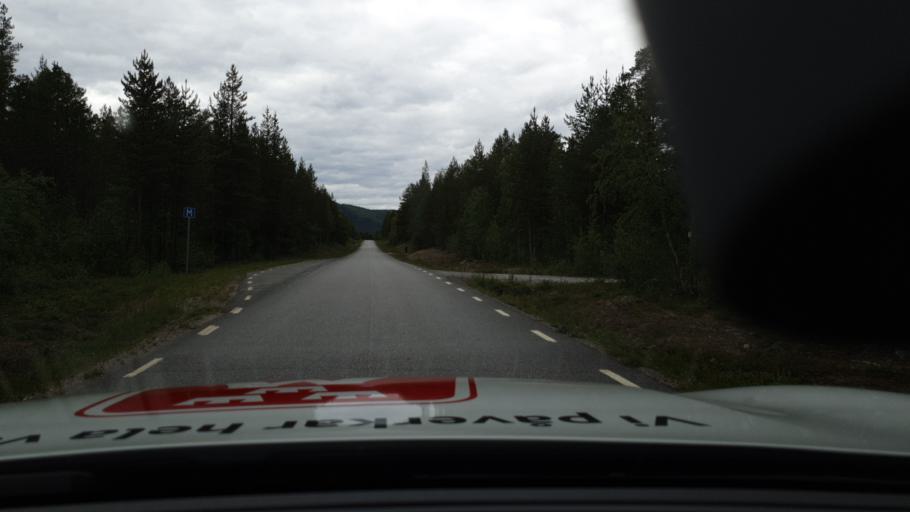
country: SE
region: Norrbotten
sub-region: Arjeplogs Kommun
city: Arjeplog
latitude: 66.8812
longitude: 18.2444
